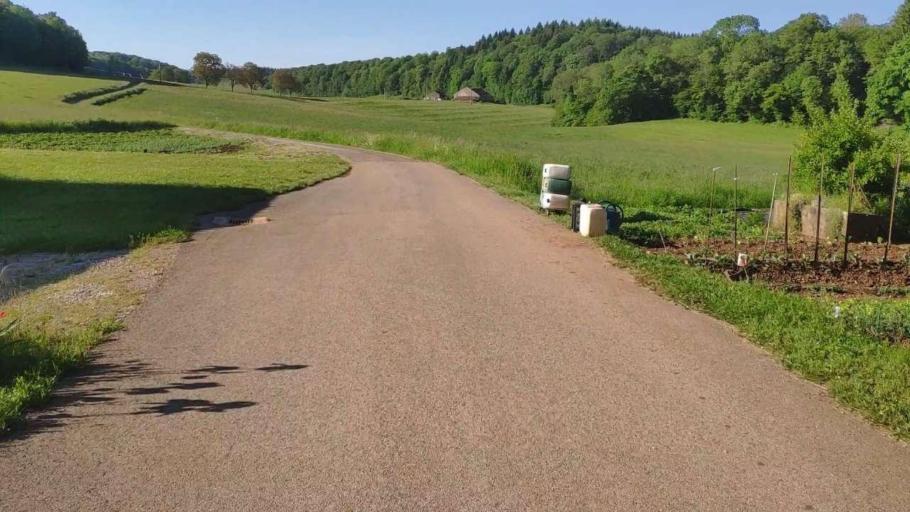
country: FR
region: Franche-Comte
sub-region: Departement du Jura
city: Perrigny
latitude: 46.7226
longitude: 5.6133
